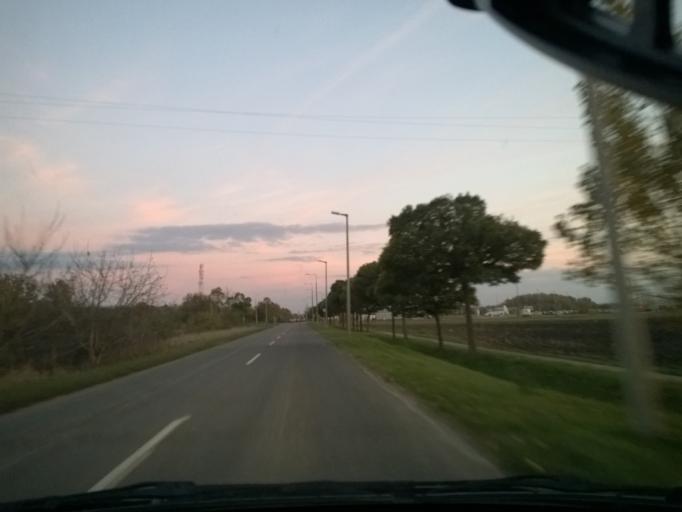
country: HU
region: Csongrad
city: Szentes
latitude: 46.6676
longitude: 20.2349
